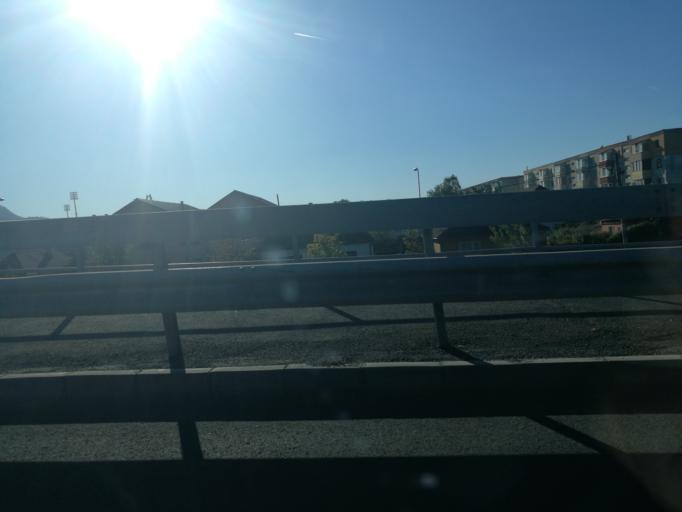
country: RO
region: Brasov
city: Brasov
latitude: 45.6686
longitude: 25.5912
